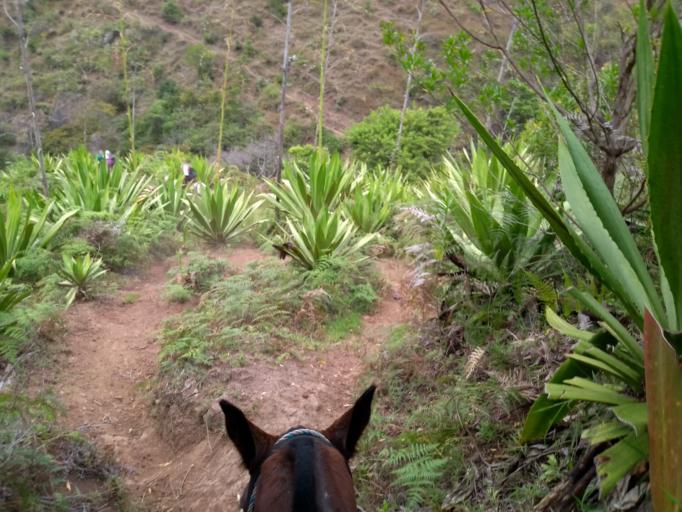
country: CO
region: Cesar
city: Manaure Balcon del Cesar
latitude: 10.1743
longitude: -73.0241
